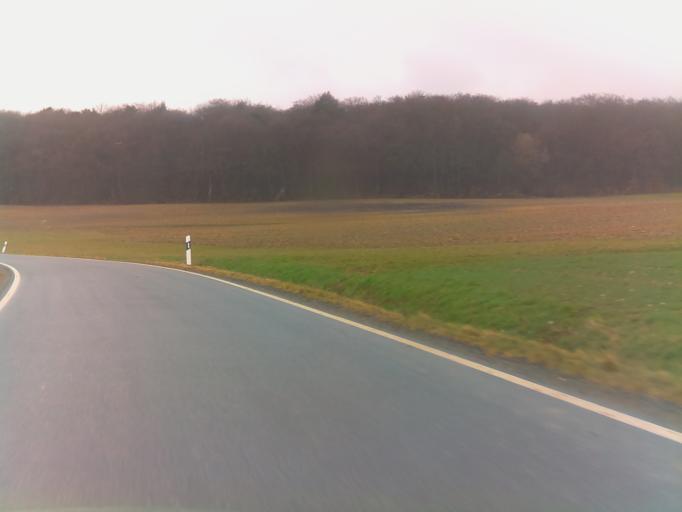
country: DE
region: Rheinland-Pfalz
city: Gosenroth
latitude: 49.8977
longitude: 7.3301
